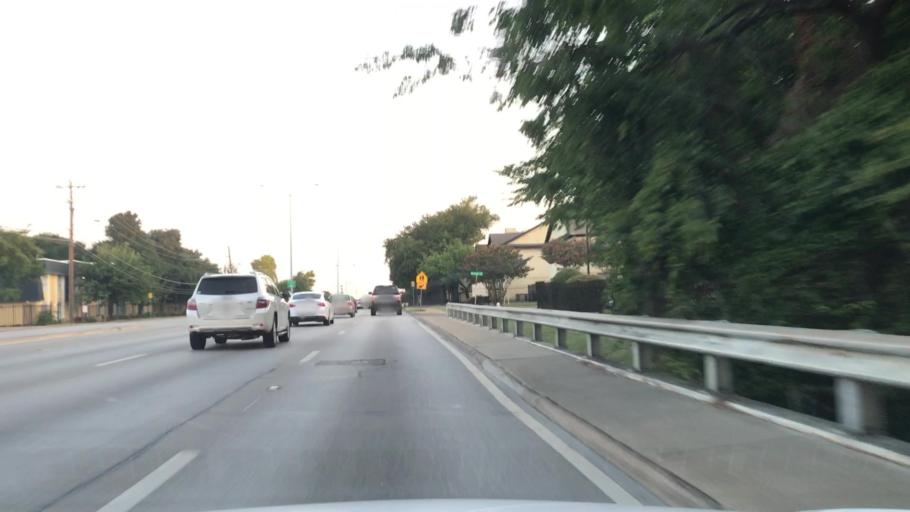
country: US
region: Texas
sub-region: Dallas County
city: Mesquite
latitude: 32.8148
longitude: -96.6876
